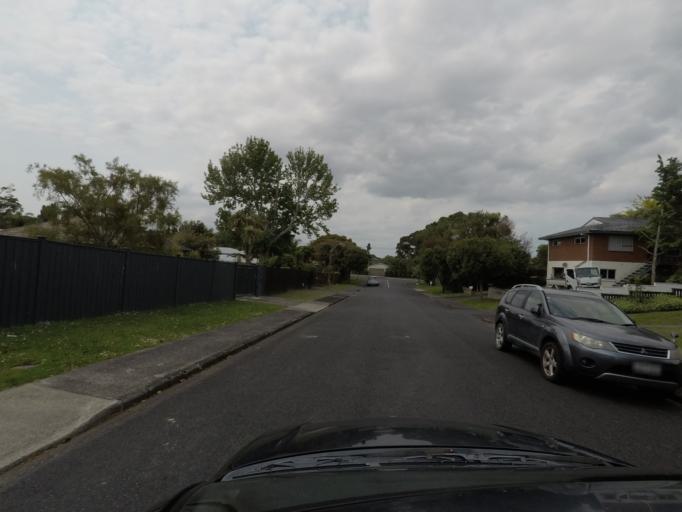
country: NZ
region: Auckland
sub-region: Auckland
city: Rosebank
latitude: -36.8407
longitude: 174.6348
